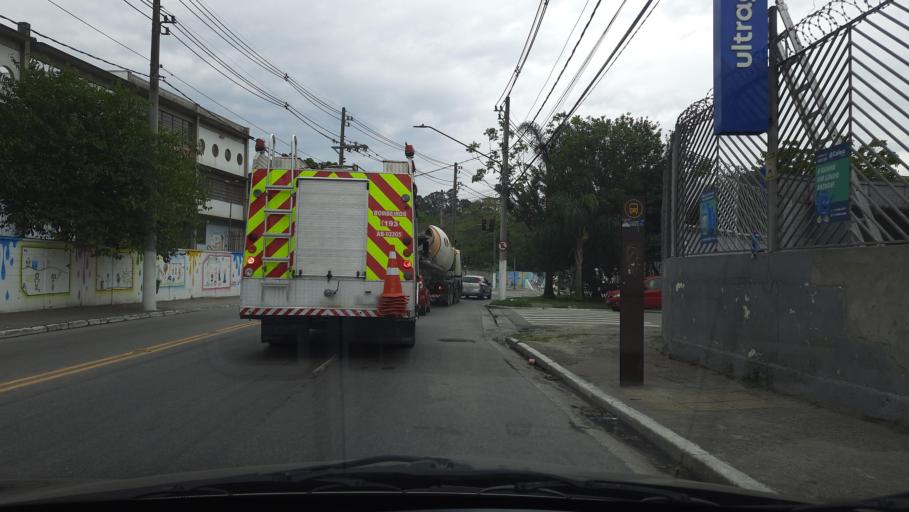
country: BR
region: Sao Paulo
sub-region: Caieiras
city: Caieiras
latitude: -23.4468
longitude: -46.7315
